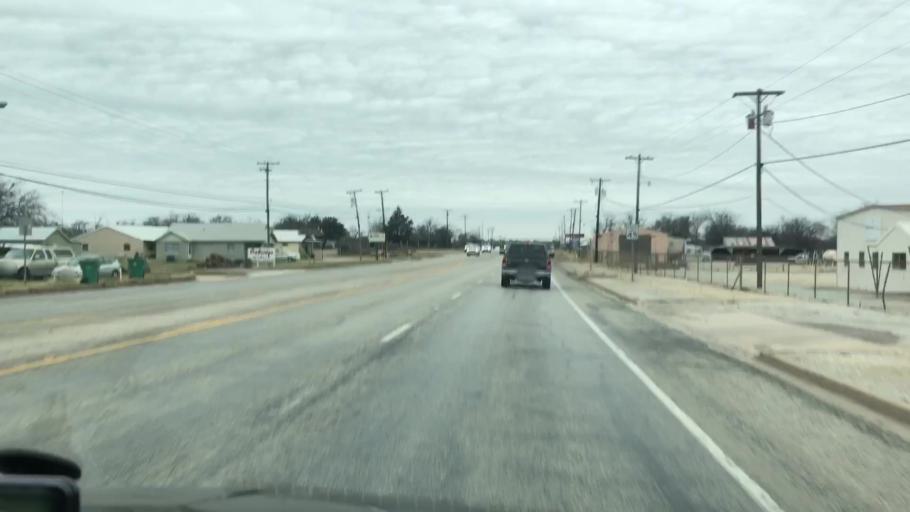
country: US
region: Texas
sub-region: Jack County
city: Jacksboro
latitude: 33.2061
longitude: -98.1539
